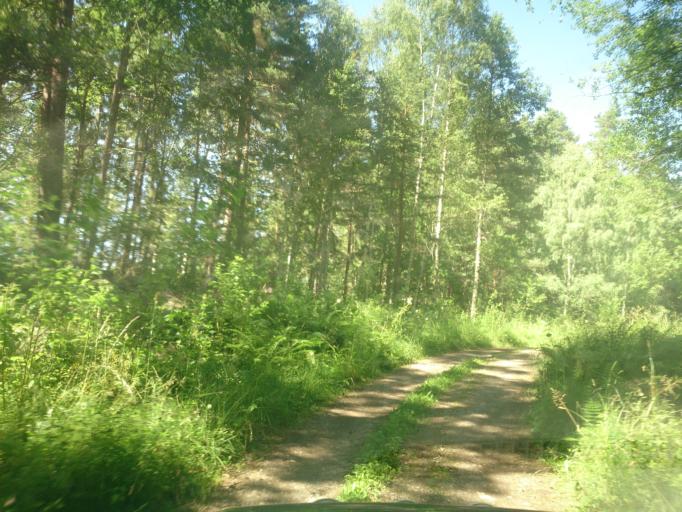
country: SE
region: OEstergoetland
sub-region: Atvidabergs Kommun
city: Atvidaberg
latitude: 58.2436
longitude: 15.9655
